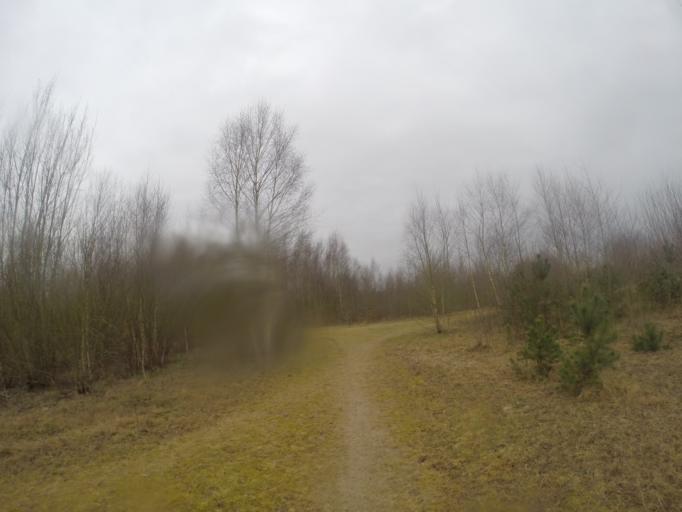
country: NL
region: Gelderland
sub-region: Gemeente Bronckhorst
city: Zelhem
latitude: 52.0182
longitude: 6.3297
